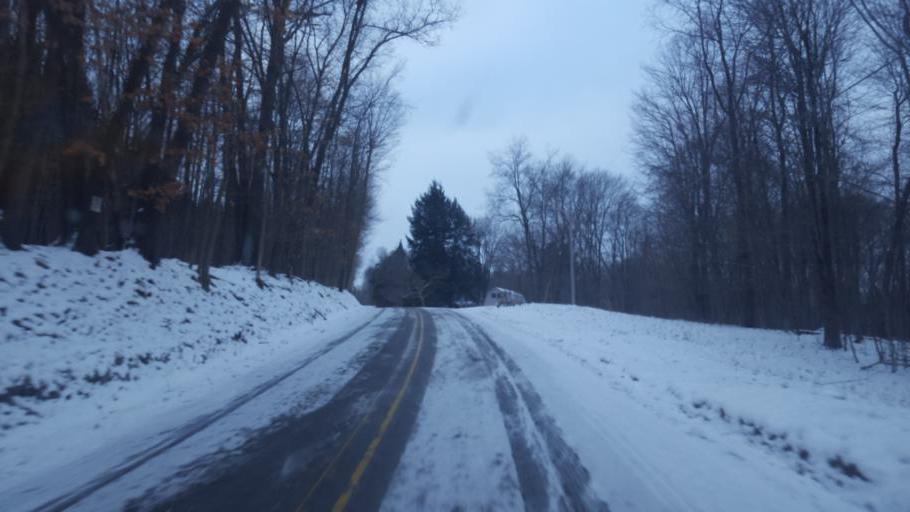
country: US
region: Pennsylvania
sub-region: Venango County
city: Sugarcreek
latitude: 41.4146
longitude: -79.9954
